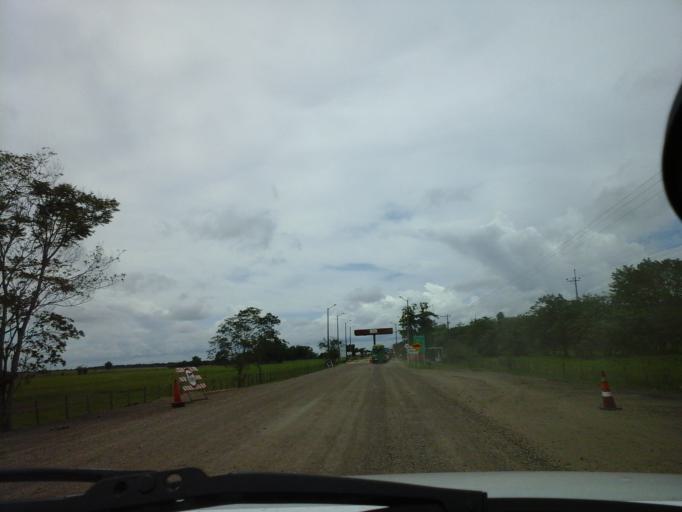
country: CO
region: Meta
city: Puerto Lopez
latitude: 4.1127
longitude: -72.8360
